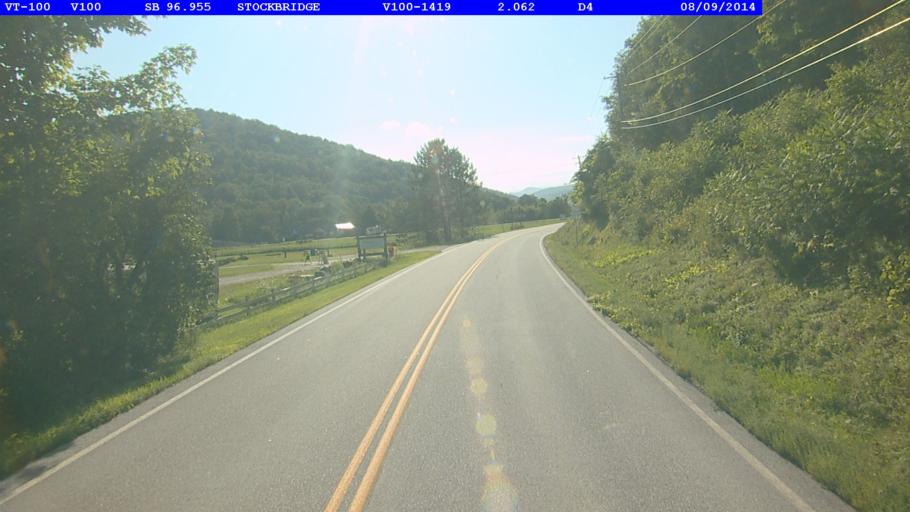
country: US
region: Vermont
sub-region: Orange County
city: Randolph
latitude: 43.7739
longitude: -72.7593
